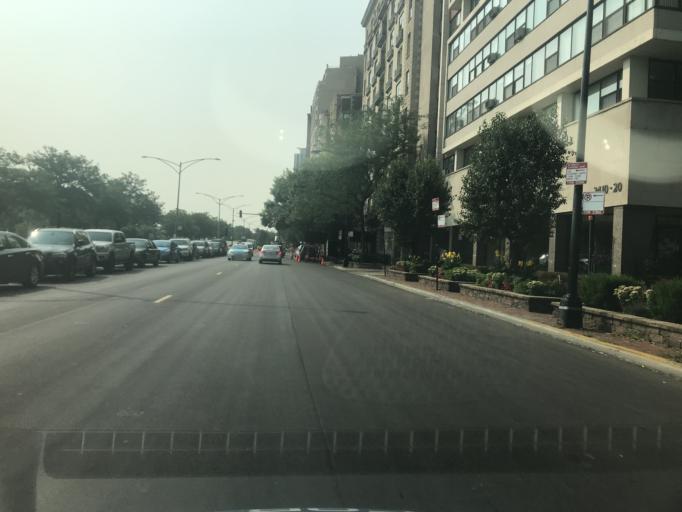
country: US
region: Illinois
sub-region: Cook County
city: Chicago
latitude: 41.9444
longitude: -87.6410
